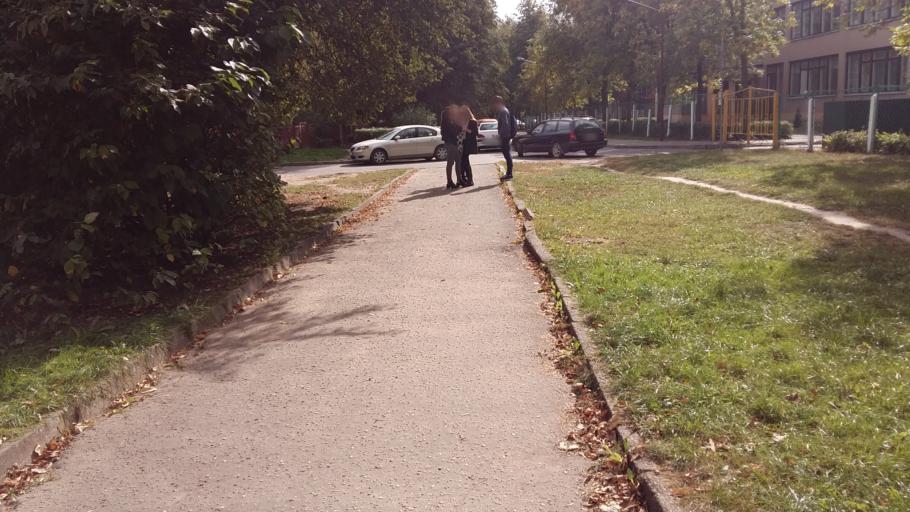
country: BY
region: Grodnenskaya
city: Hrodna
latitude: 53.6919
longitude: 23.8048
